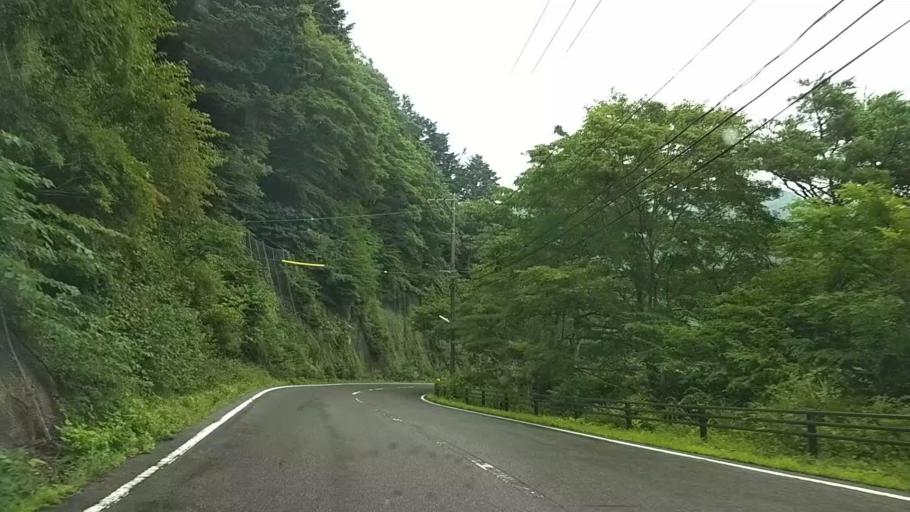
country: JP
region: Yamanashi
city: Fujikawaguchiko
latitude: 35.4881
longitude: 138.6045
